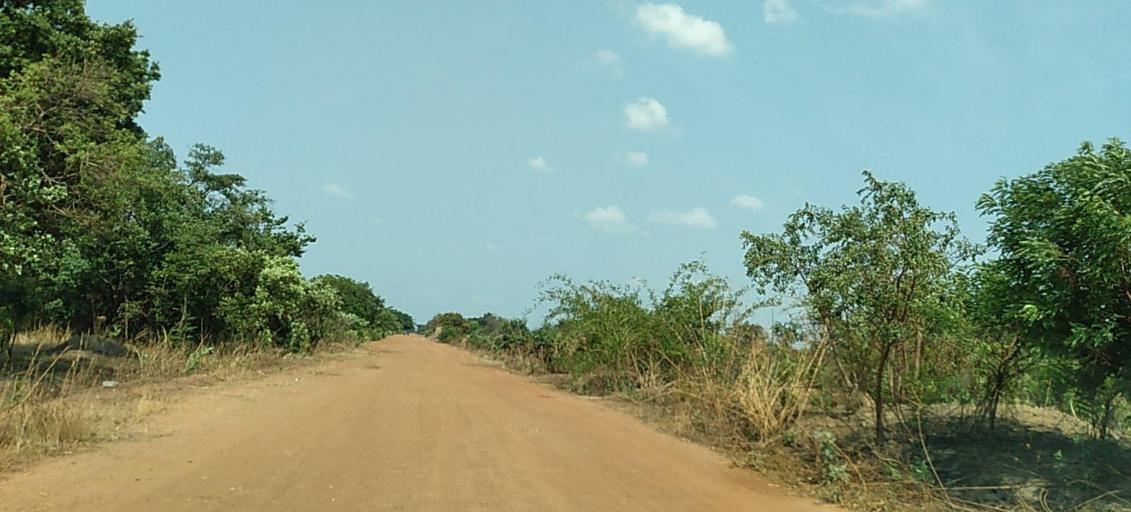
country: ZM
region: Copperbelt
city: Luanshya
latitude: -13.0913
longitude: 28.2893
